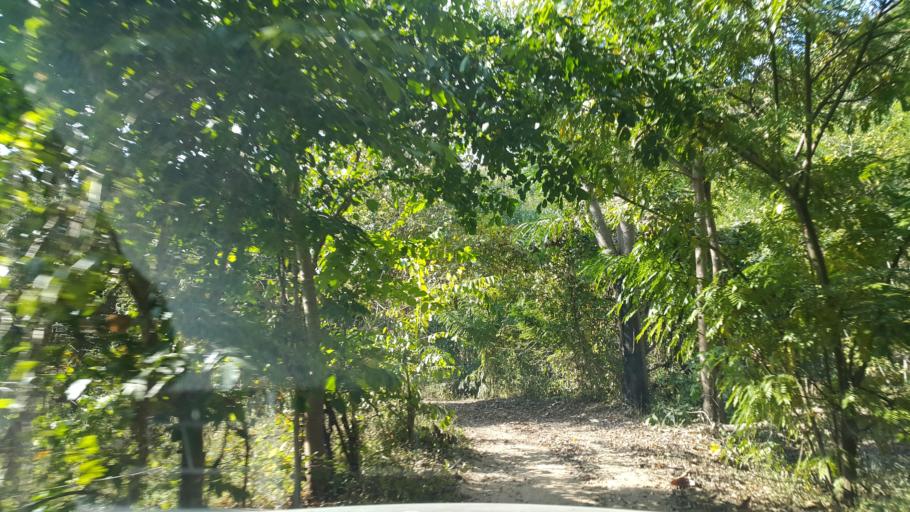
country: TH
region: Lamphun
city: Ban Thi
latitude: 18.5749
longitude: 99.1707
